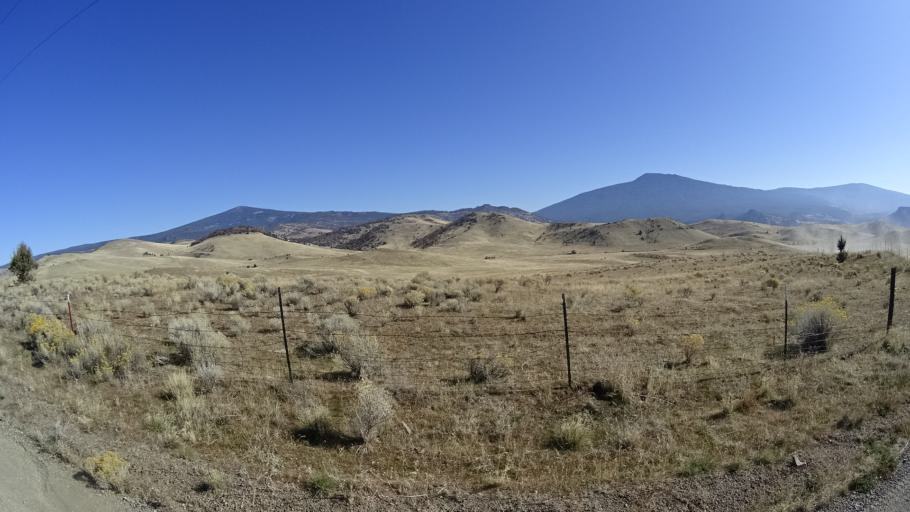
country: US
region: California
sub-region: Siskiyou County
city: Montague
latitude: 41.7696
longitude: -122.3592
